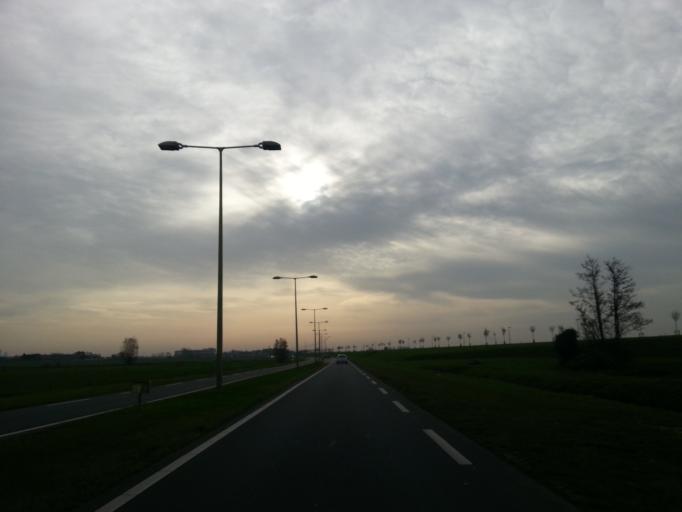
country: NL
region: South Holland
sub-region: Gemeente Lansingerland
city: Berkel en Rodenrijs
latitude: 51.9920
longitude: 4.4505
